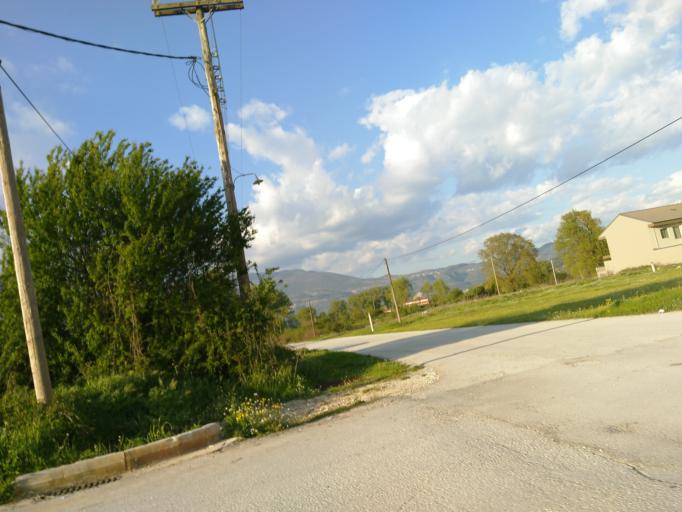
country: GR
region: Epirus
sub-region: Nomos Ioanninon
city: Katsikas
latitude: 39.6261
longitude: 20.8879
